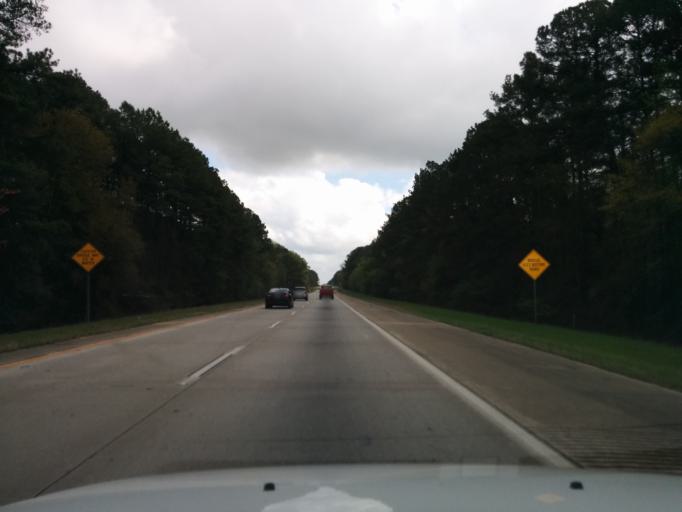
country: US
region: Georgia
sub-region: Bulloch County
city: Statesboro
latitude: 32.2917
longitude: -81.8099
